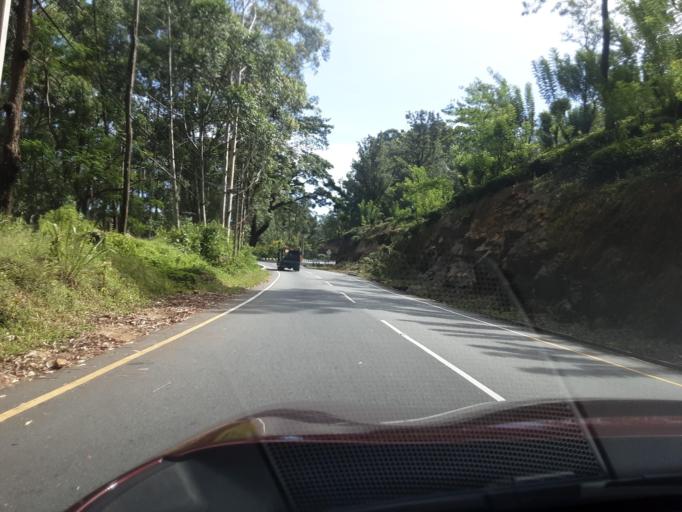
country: LK
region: Uva
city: Badulla
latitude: 6.9587
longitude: 81.1089
